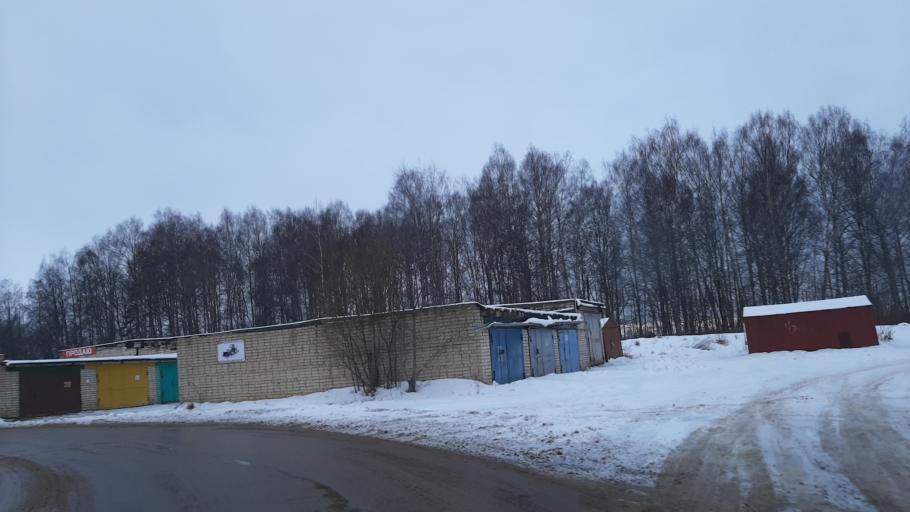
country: RU
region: Kostroma
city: Volgorechensk
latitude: 57.4444
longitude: 41.1450
